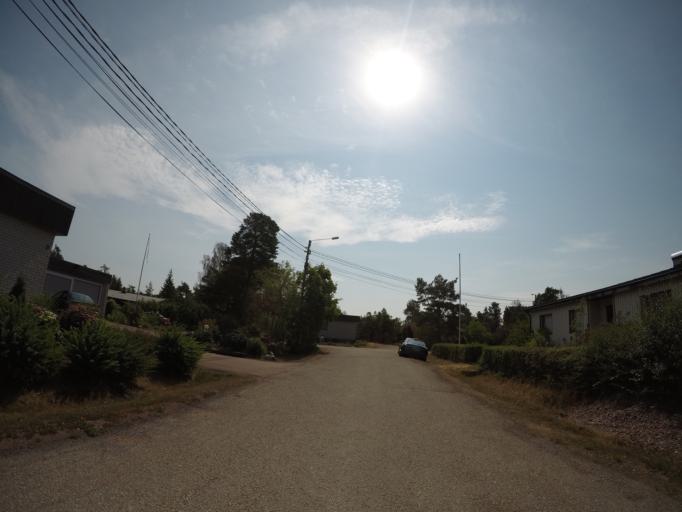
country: AX
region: Alands landsbygd
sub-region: Saltvik
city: Saltvik
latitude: 60.2320
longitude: 20.0004
